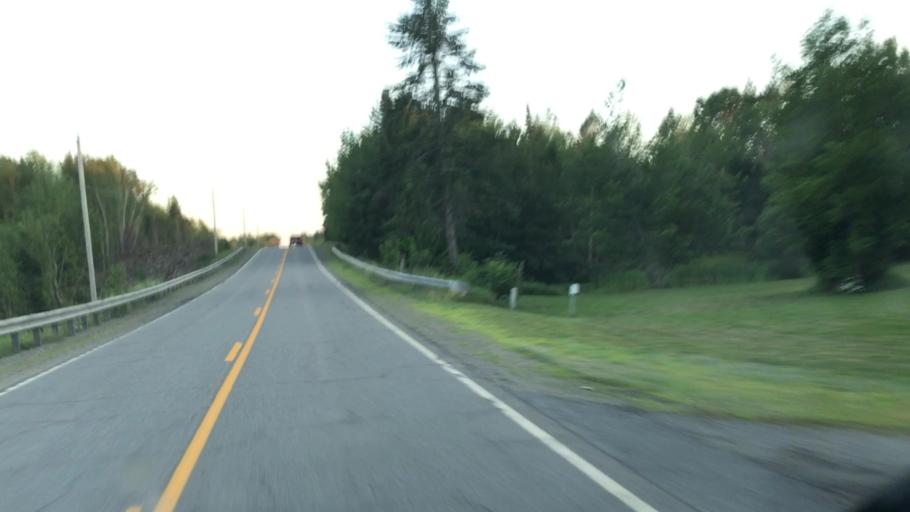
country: US
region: Maine
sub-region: Penobscot County
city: Medway
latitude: 45.6028
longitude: -68.3086
